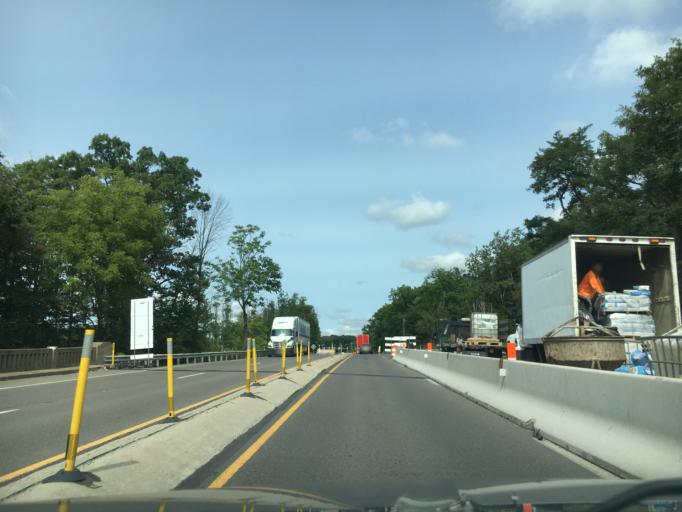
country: US
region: Pennsylvania
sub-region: Schuylkill County
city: Hometown
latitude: 40.8298
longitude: -75.9858
